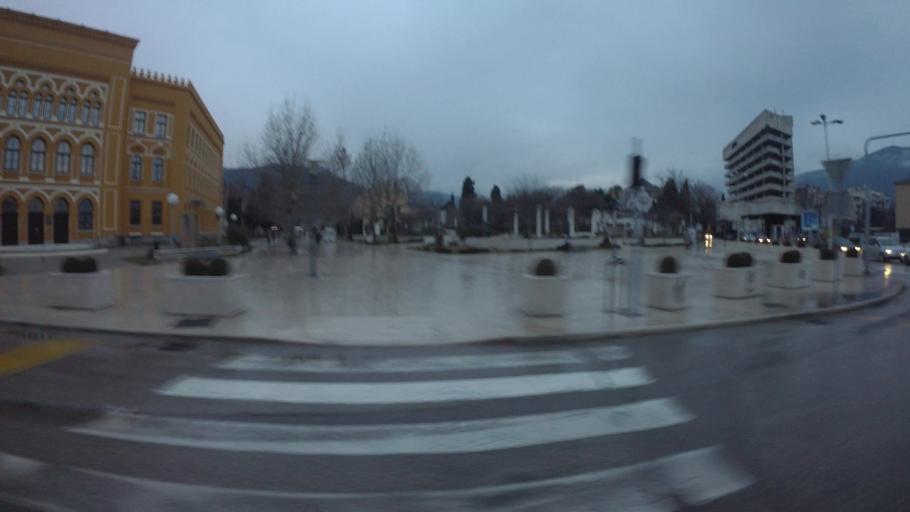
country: BA
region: Federation of Bosnia and Herzegovina
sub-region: Hercegovacko-Bosanski Kanton
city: Mostar
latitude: 43.3436
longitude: 17.8076
